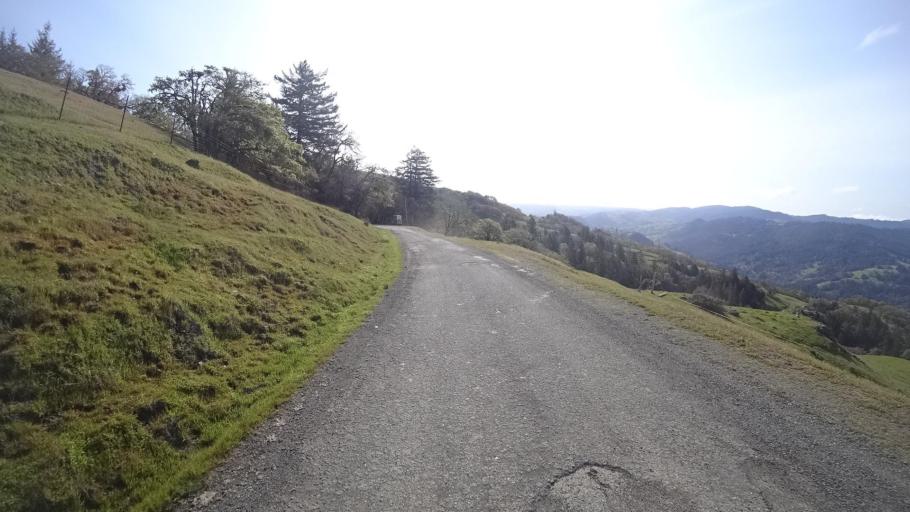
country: US
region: California
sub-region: Humboldt County
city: Hydesville
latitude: 40.6421
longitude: -123.9136
